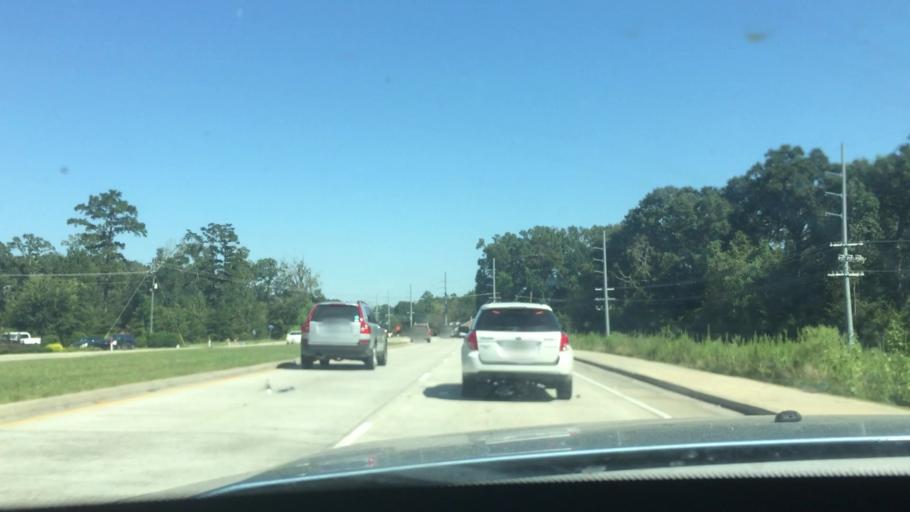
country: US
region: Louisiana
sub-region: East Baton Rouge Parish
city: Shenandoah
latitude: 30.4264
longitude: -91.0124
